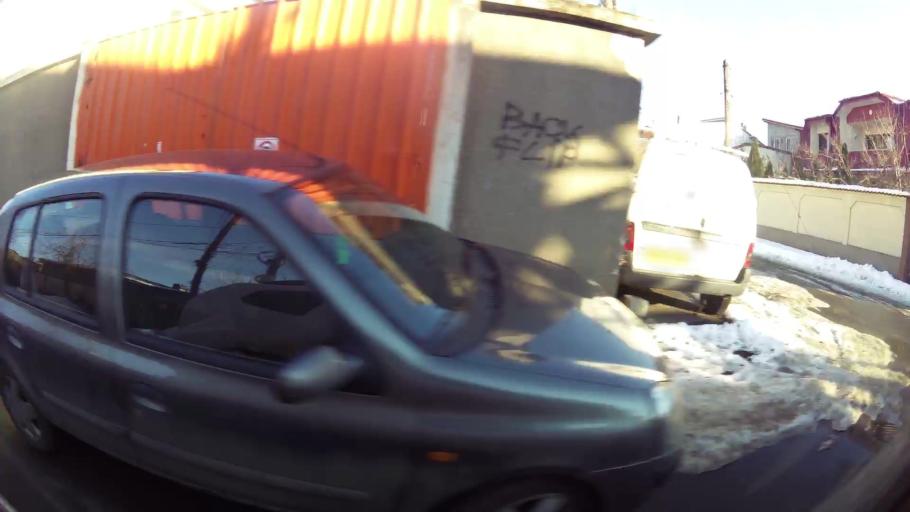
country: RO
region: Bucuresti
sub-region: Municipiul Bucuresti
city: Bucuresti
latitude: 44.3970
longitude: 26.0915
